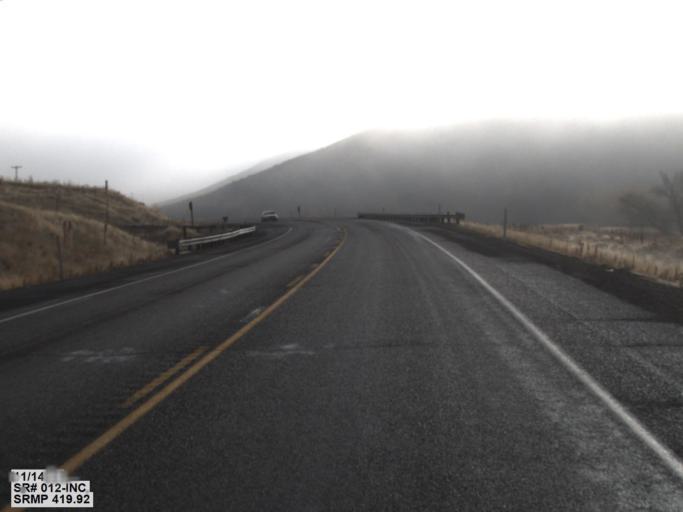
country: US
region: Washington
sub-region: Asotin County
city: Clarkston Heights-Vineland
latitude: 46.4272
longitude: -117.3021
